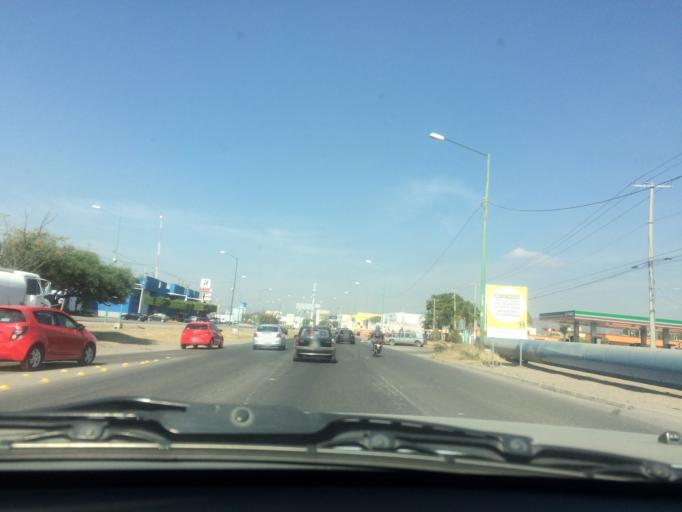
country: MX
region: Guanajuato
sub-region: Leon
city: Medina
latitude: 21.1500
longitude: -101.6348
